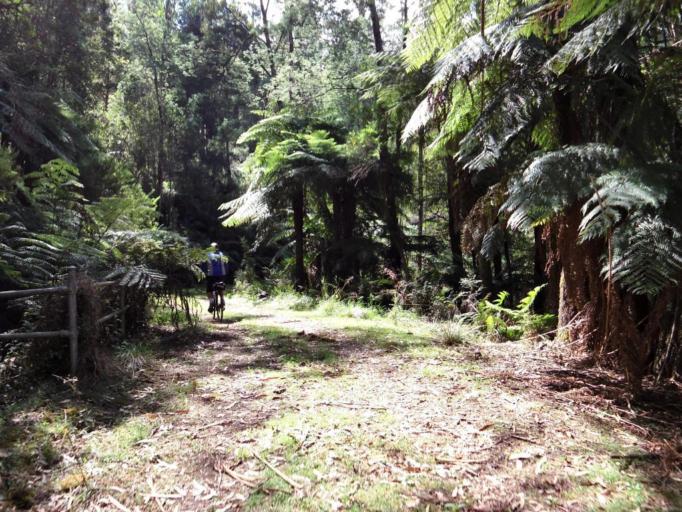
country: AU
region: Victoria
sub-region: Yarra Ranges
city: Millgrove
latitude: -37.6901
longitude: 145.8046
